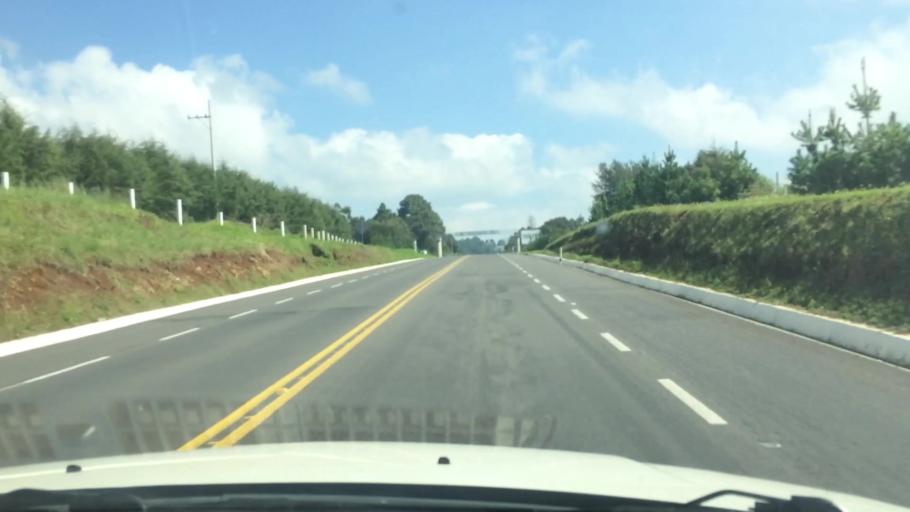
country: MX
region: Mexico
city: Amanalco de Becerra
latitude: 19.3350
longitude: -99.9957
